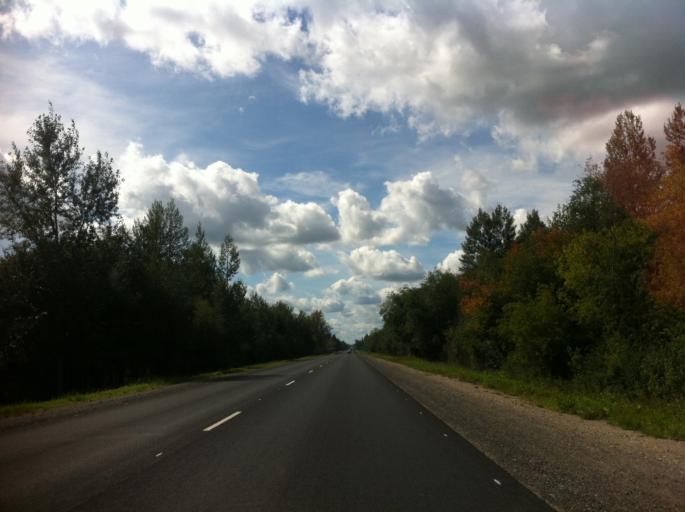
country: RU
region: Pskov
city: Izborsk
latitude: 57.7538
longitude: 28.0624
